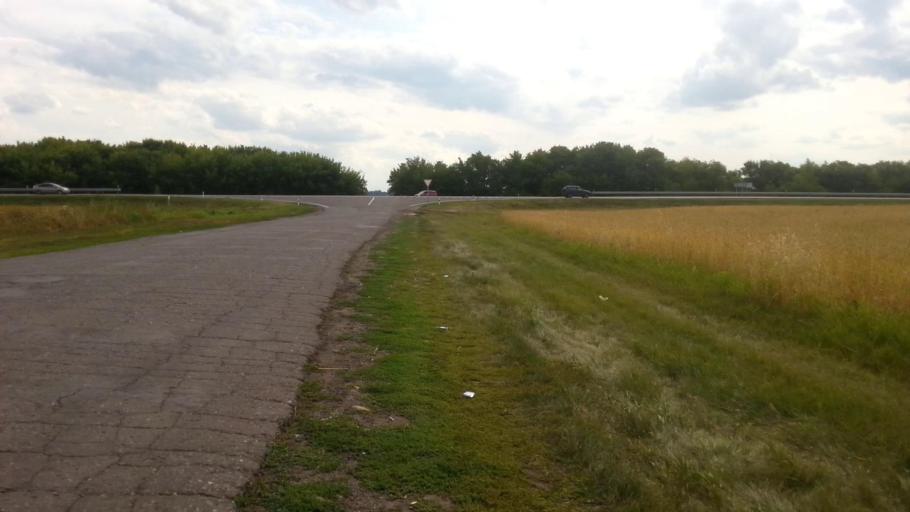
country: RU
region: Altai Krai
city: Nauchnyy Gorodok
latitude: 53.3576
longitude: 83.5082
